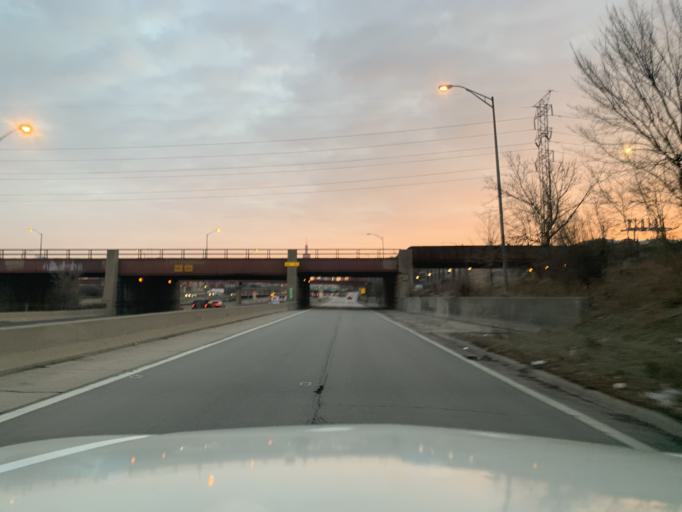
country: US
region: Illinois
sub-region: Cook County
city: Chicago
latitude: 41.8751
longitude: -87.6922
